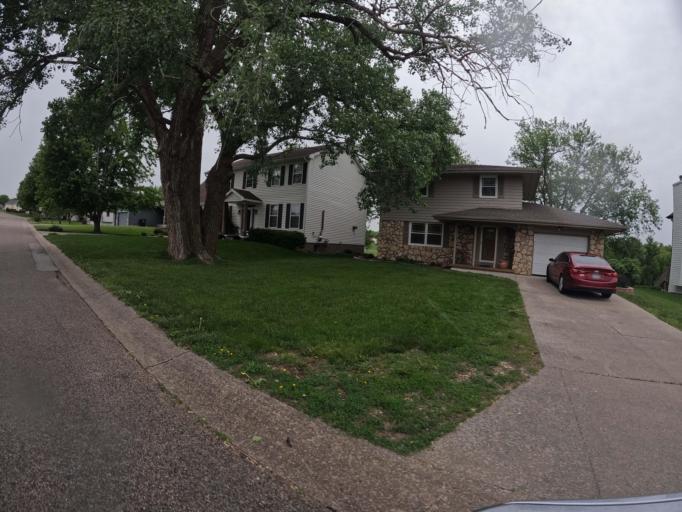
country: US
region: Nebraska
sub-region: Sarpy County
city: Offutt Air Force Base
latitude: 41.0467
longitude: -95.9722
